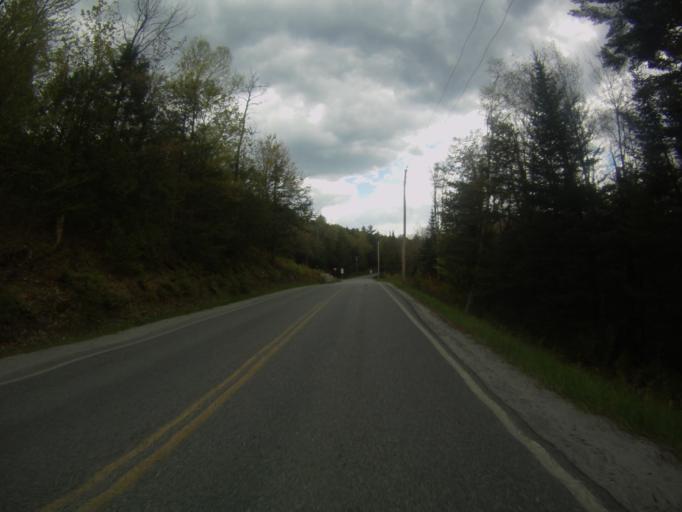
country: US
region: New York
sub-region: Essex County
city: Mineville
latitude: 44.0550
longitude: -73.5300
